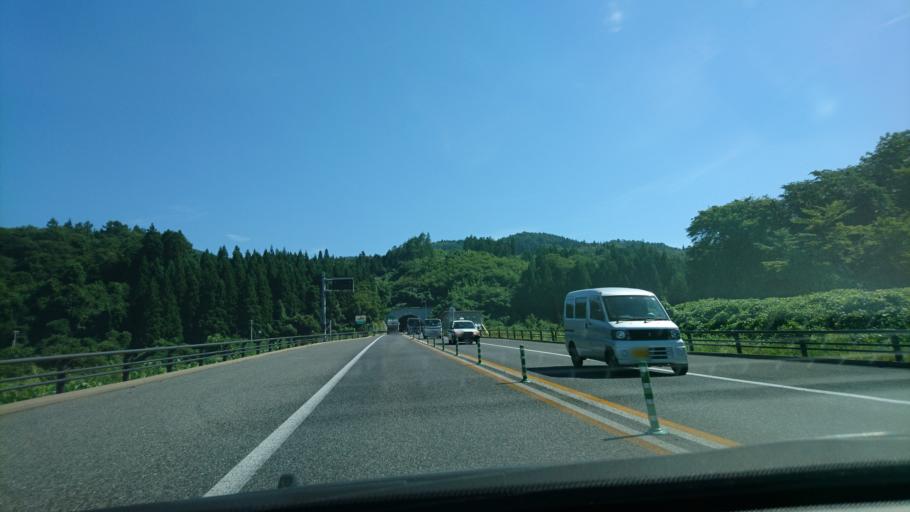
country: JP
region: Iwate
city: Kitakami
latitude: 39.2928
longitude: 141.2900
